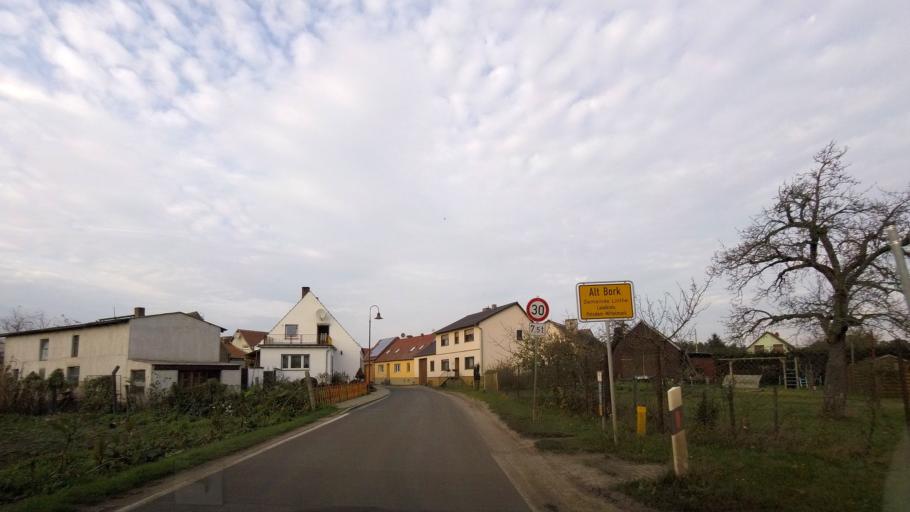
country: DE
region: Brandenburg
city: Borkheide
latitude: 52.1864
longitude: 12.8715
